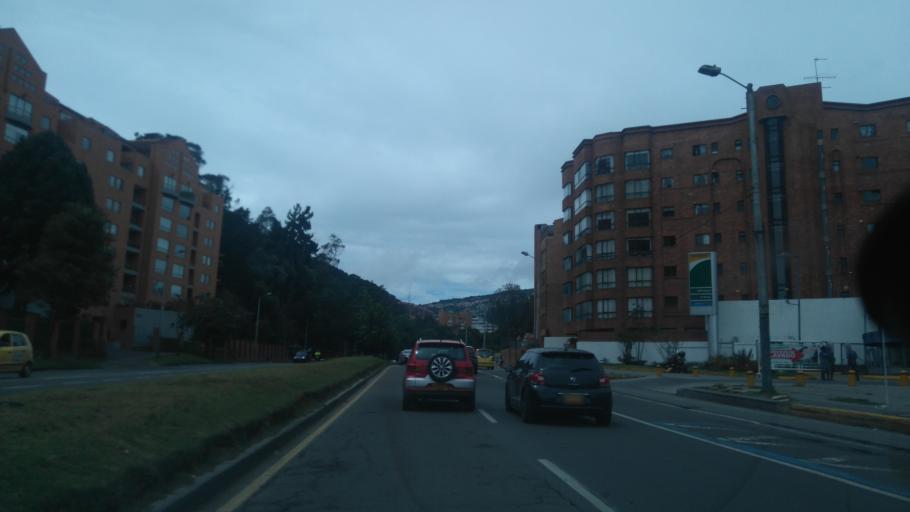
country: CO
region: Bogota D.C.
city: Barrio San Luis
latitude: 4.7114
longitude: -74.0292
